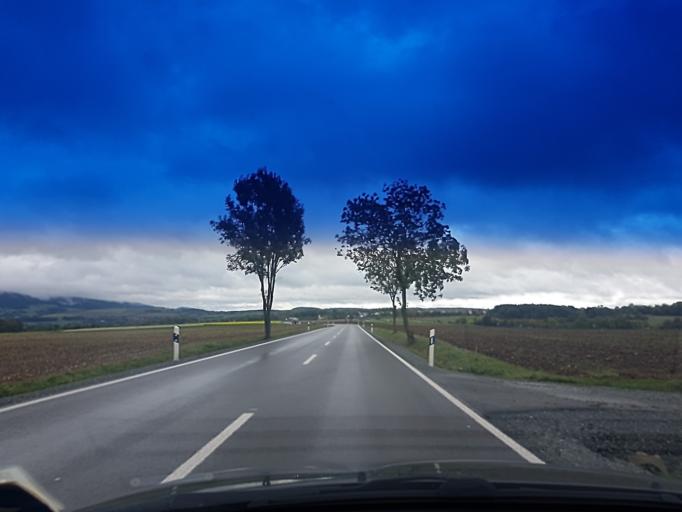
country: DE
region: Bavaria
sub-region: Upper Franconia
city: Bindlach
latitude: 50.0087
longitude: 11.6168
